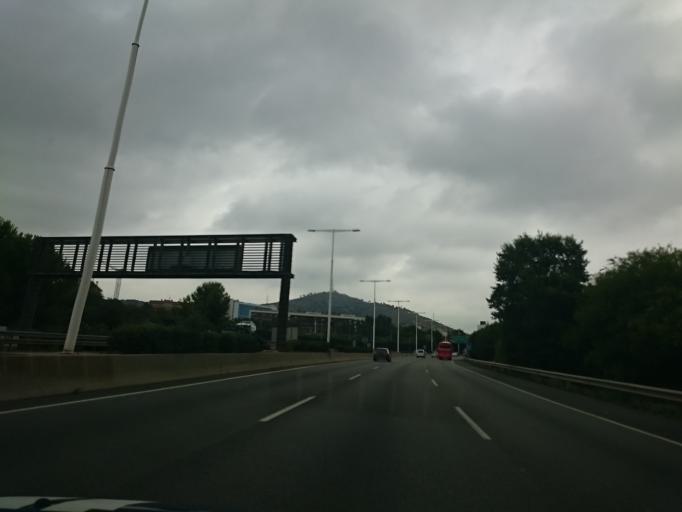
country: ES
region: Catalonia
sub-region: Provincia de Barcelona
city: Esplugues de Llobregat
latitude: 41.3742
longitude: 2.0946
